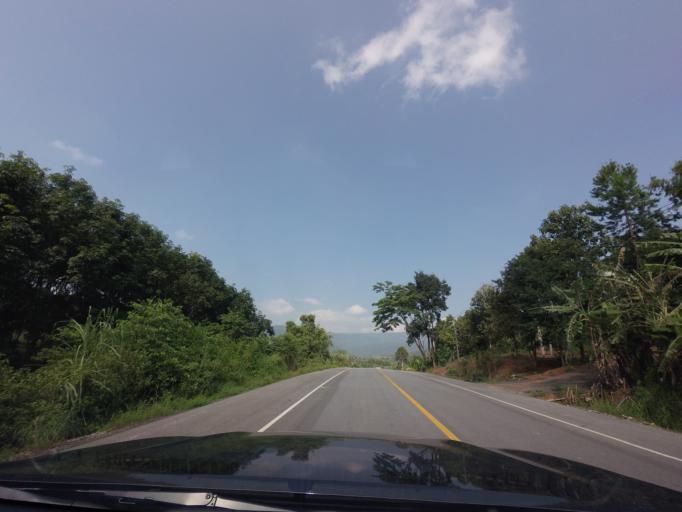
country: TH
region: Loei
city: Na Haeo
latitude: 17.4969
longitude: 101.0227
